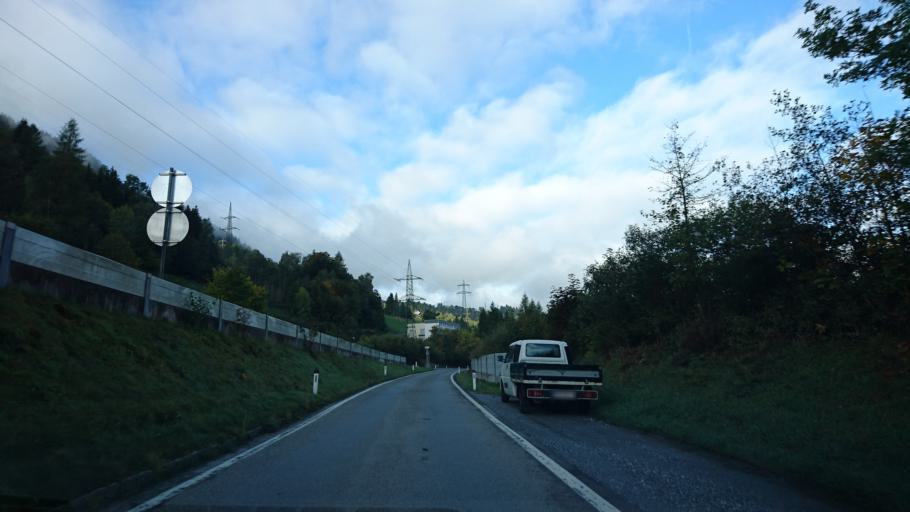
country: AT
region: Salzburg
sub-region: Politischer Bezirk Zell am See
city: Lend
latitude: 47.2945
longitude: 13.0545
